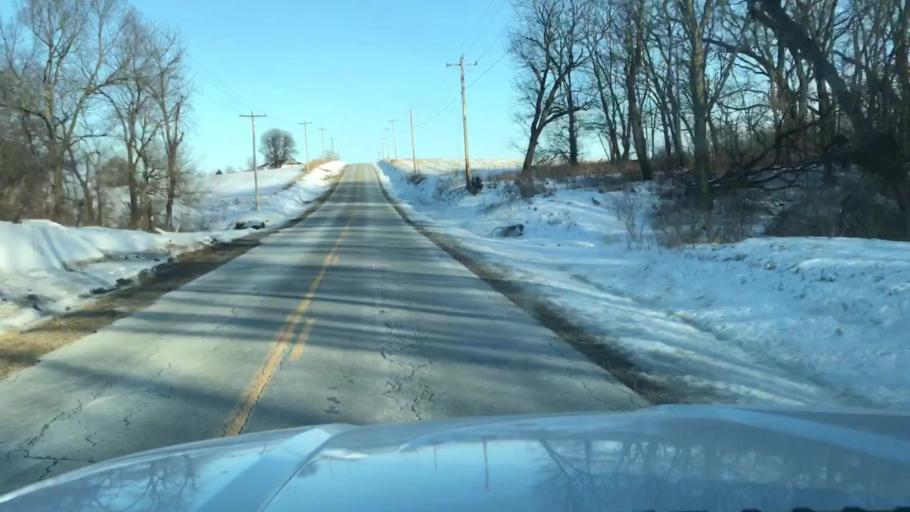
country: US
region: Missouri
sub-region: Andrew County
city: Savannah
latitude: 40.0247
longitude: -94.8908
